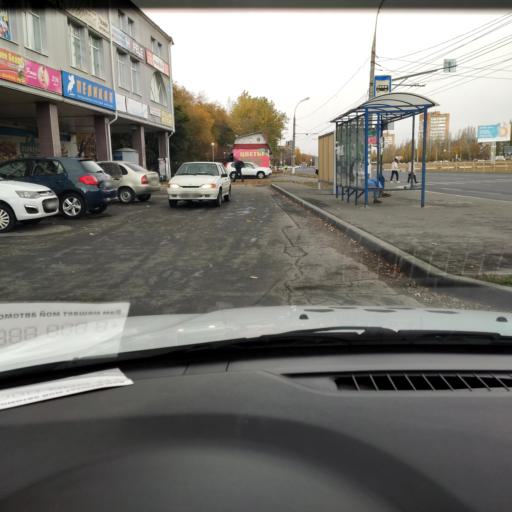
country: RU
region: Samara
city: Tol'yatti
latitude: 53.5161
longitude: 49.2936
